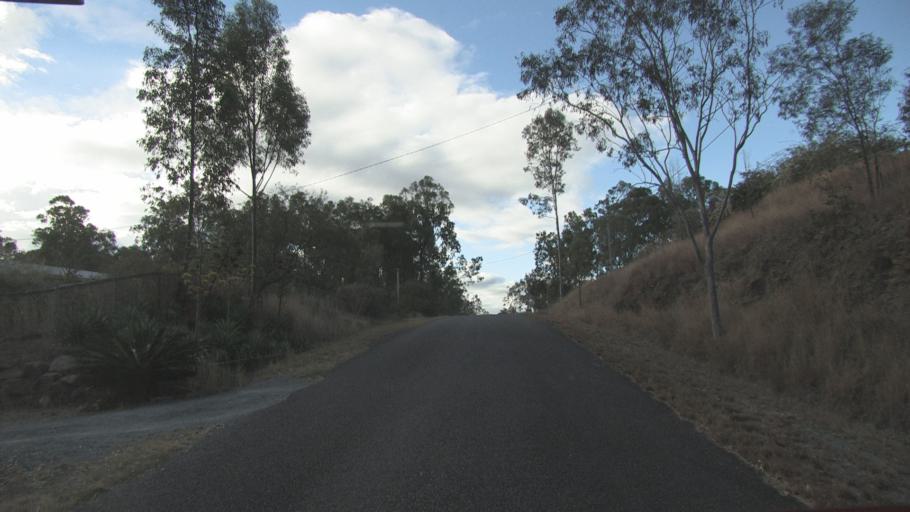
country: AU
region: Queensland
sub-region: Logan
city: Cedar Vale
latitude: -27.9044
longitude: 153.0730
